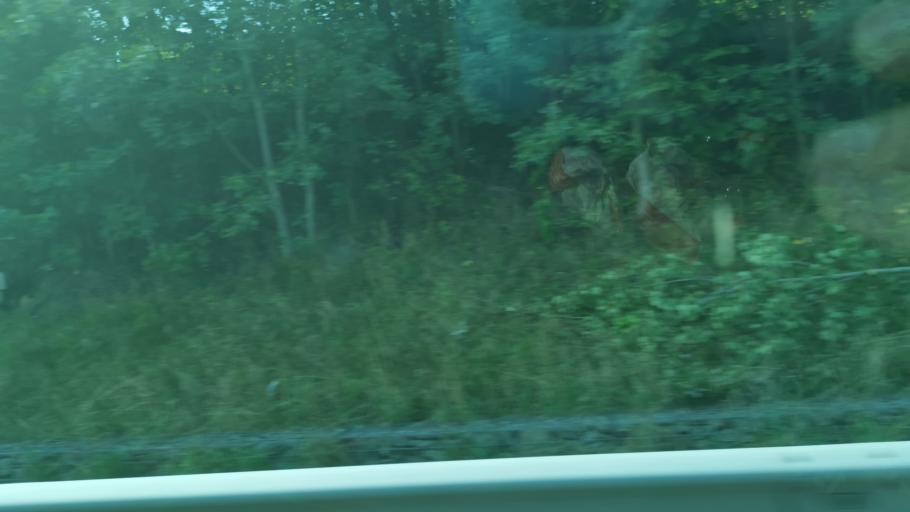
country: DE
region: Bavaria
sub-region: Upper Palatinate
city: Chamerau
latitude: 49.2070
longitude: 12.7290
